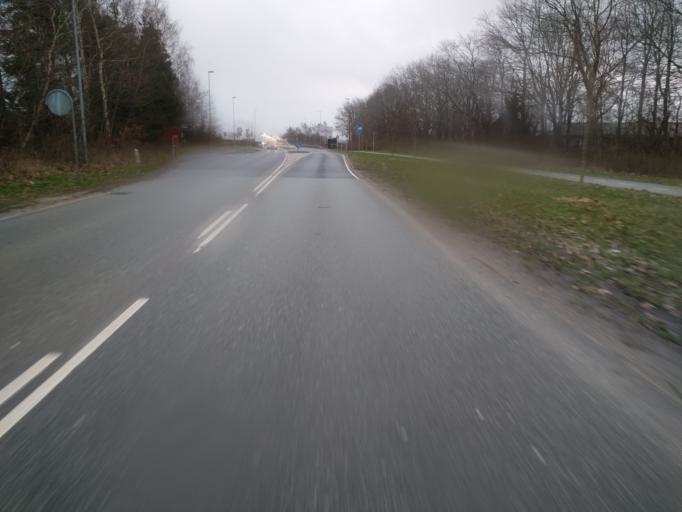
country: DK
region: Central Jutland
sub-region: Viborg Kommune
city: Viborg
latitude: 56.4545
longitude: 9.4458
